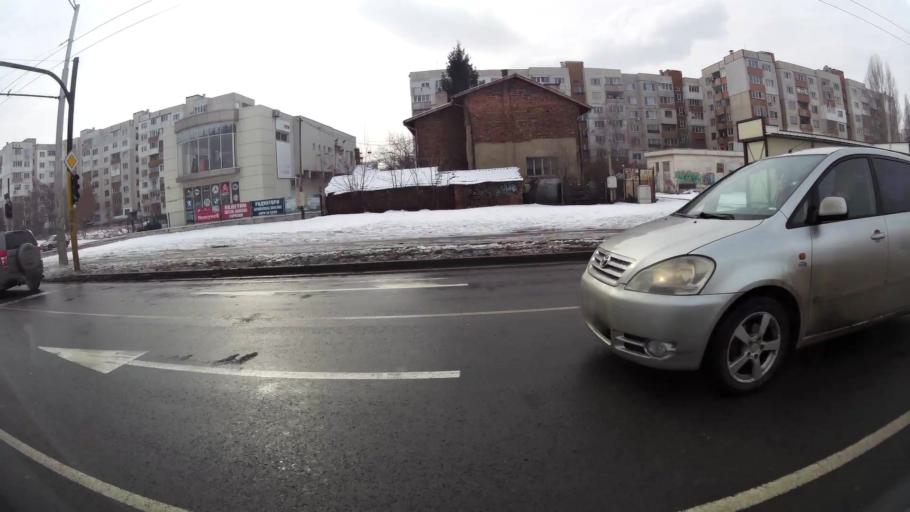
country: BG
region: Sofia-Capital
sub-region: Stolichna Obshtina
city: Sofia
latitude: 42.7106
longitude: 23.3841
